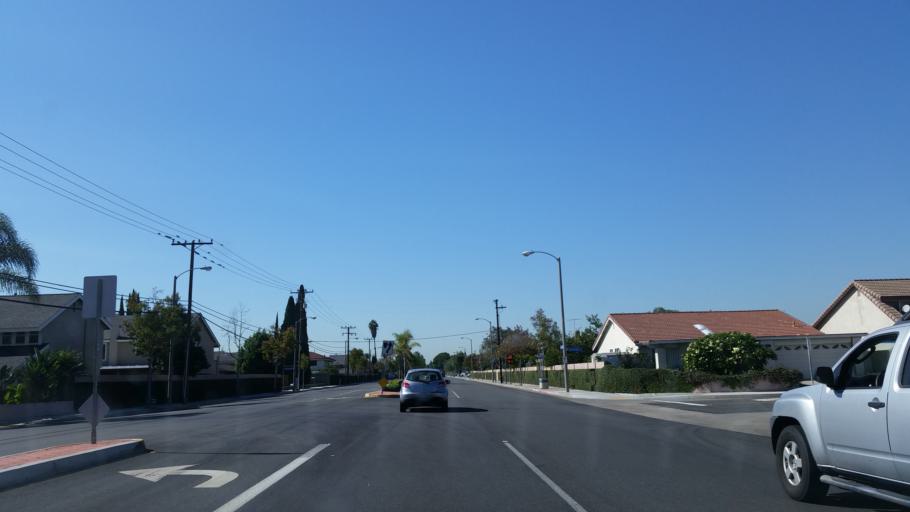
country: US
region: California
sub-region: Orange County
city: La Palma
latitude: 33.8463
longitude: -118.0481
